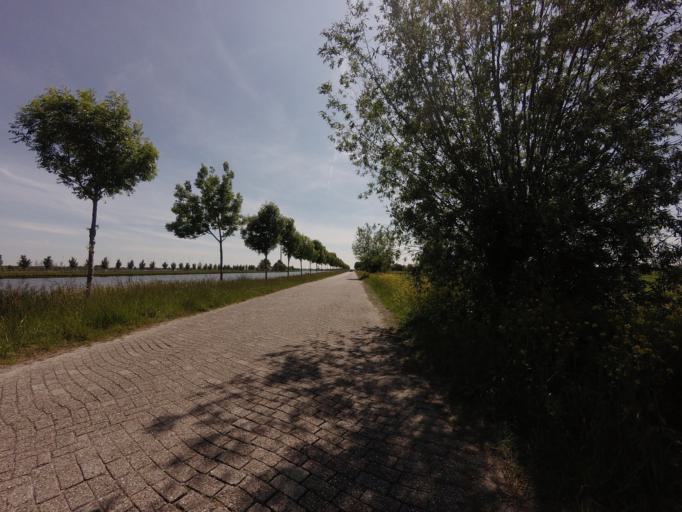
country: NL
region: Utrecht
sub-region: Gemeente Houten
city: Houten
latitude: 52.0180
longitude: 5.1408
